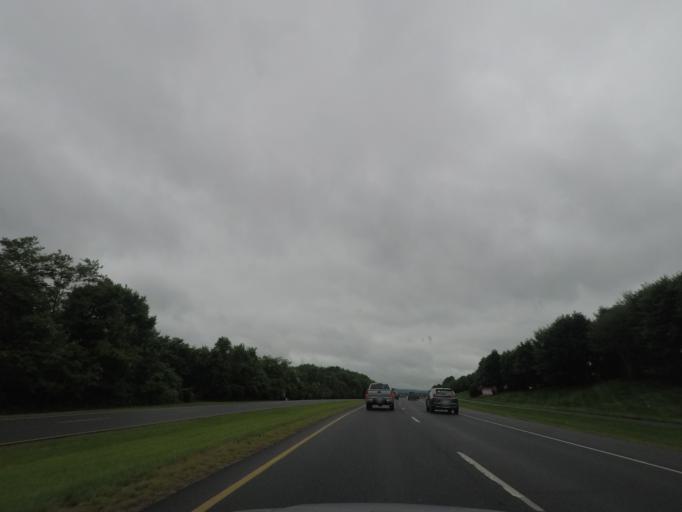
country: US
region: Virginia
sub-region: Prince William County
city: Haymarket
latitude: 38.8395
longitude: -77.6352
